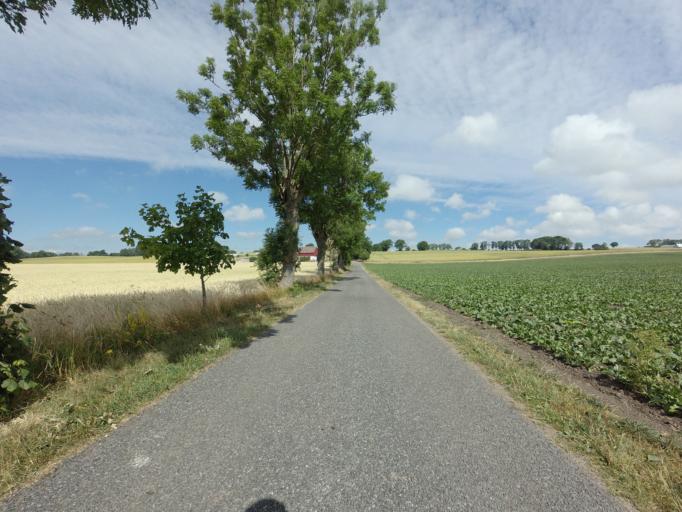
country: SE
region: Skane
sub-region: Simrishamns Kommun
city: Simrishamn
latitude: 55.4895
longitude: 14.3101
